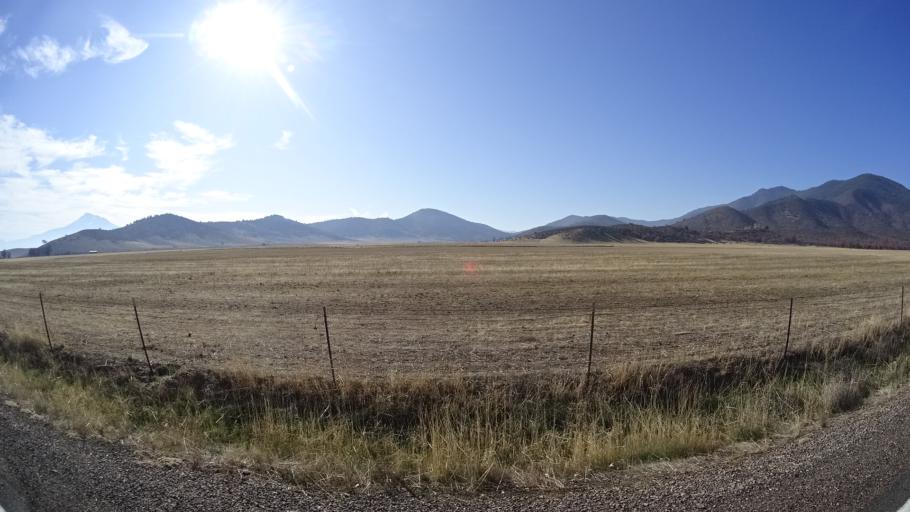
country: US
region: California
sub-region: Siskiyou County
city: Montague
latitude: 41.6547
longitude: -122.5676
